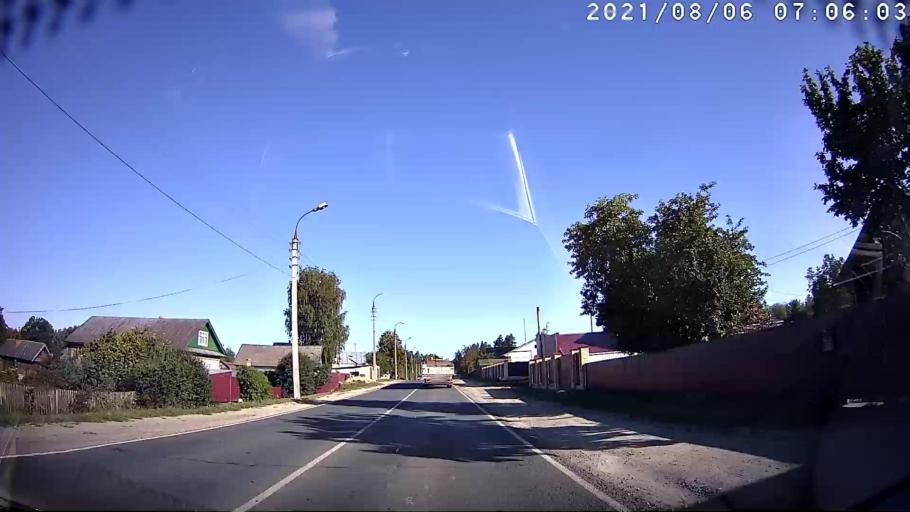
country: RU
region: Mariy-El
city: Yoshkar-Ola
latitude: 56.5566
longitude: 47.9832
